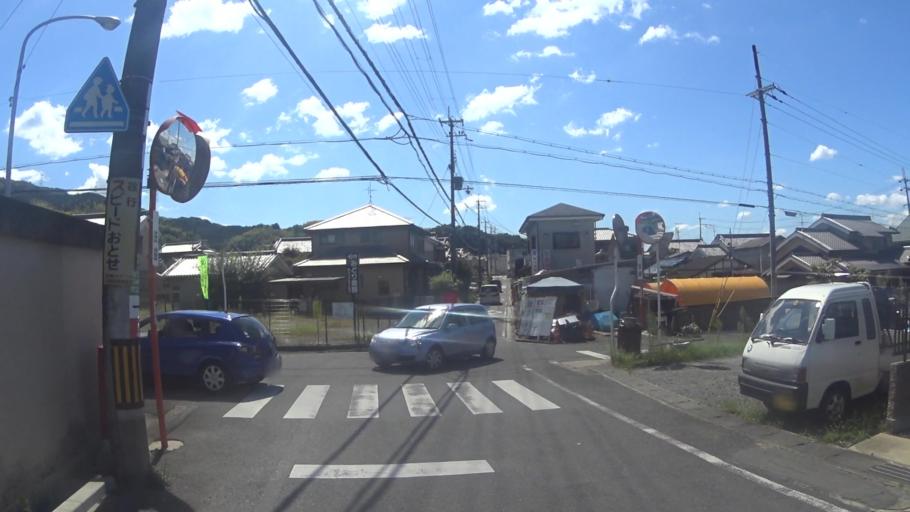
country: JP
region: Kyoto
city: Tanabe
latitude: 34.8168
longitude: 135.8083
